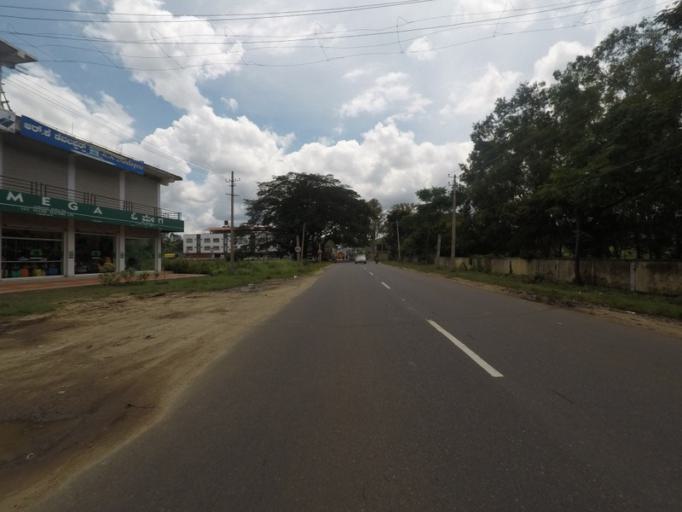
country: IN
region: Karnataka
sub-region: Kodagu
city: Kushalnagar
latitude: 12.4509
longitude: 75.9445
